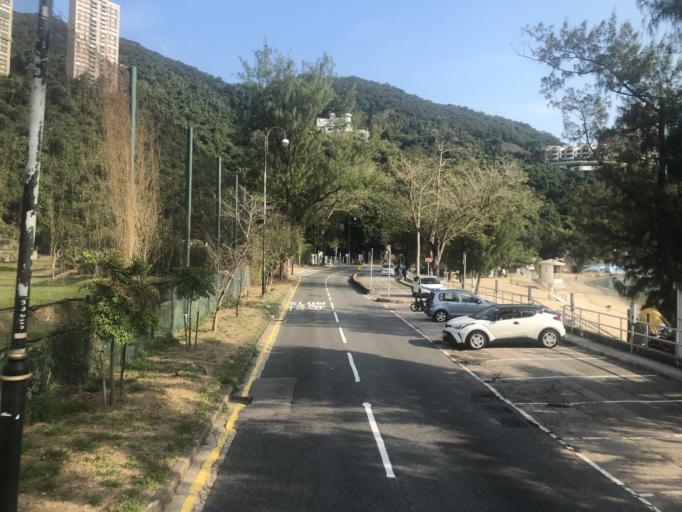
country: HK
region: Wanchai
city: Wan Chai
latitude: 22.2450
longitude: 114.1875
